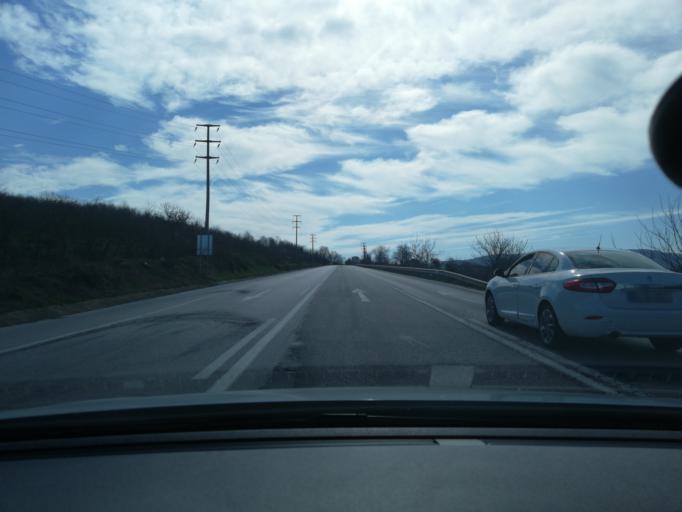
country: TR
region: Duzce
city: Akcakoca
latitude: 41.0779
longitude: 31.1063
